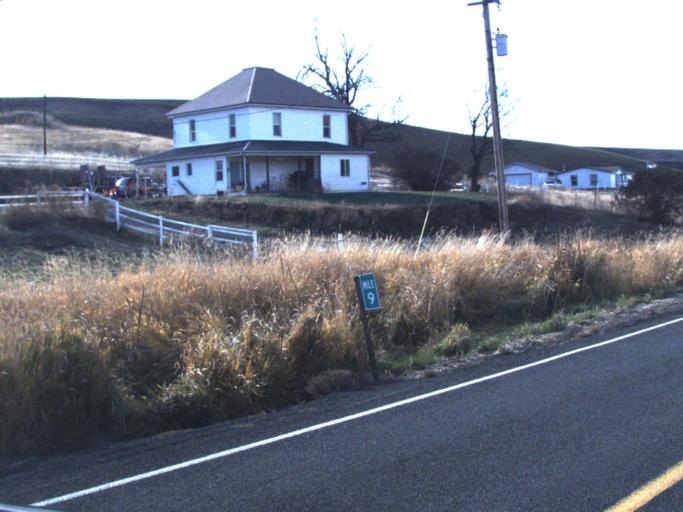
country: US
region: Washington
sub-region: Whitman County
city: Colfax
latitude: 46.7674
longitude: -117.4079
